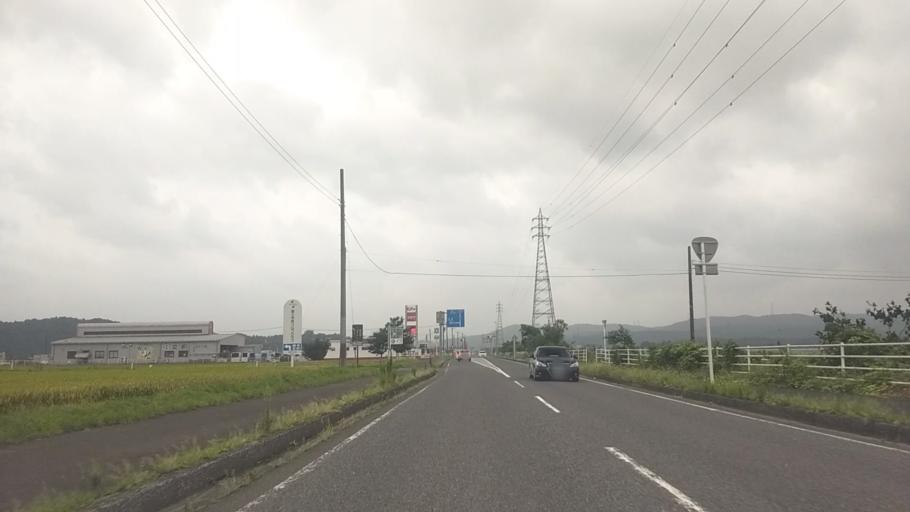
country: JP
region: Chiba
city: Kisarazu
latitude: 35.3325
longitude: 140.0549
